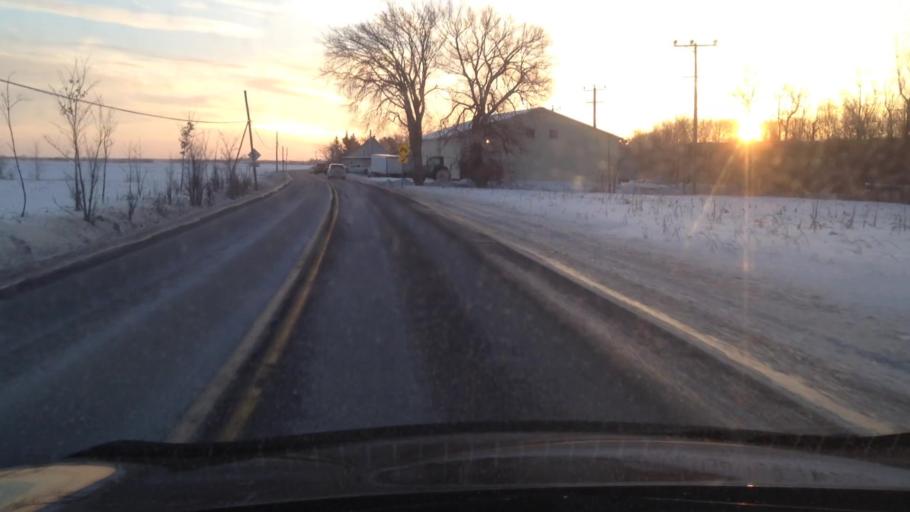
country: CA
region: Quebec
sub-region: Lanaudiere
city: Saint-Lin-Laurentides
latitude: 45.9090
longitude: -73.7437
